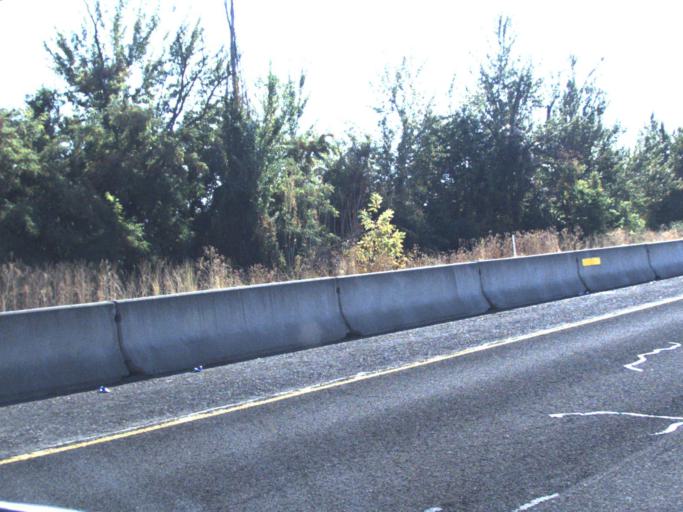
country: US
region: Washington
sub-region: Walla Walla County
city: Walla Walla
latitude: 46.0442
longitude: -118.3581
